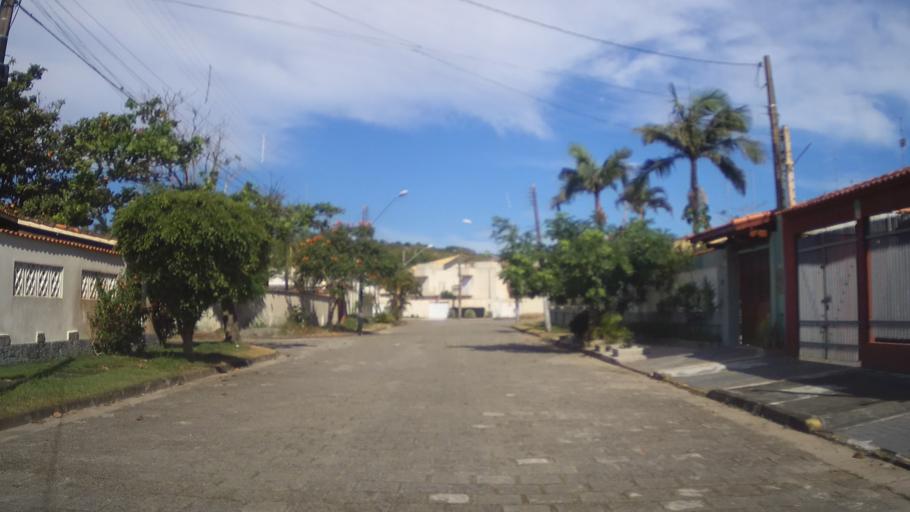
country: BR
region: Sao Paulo
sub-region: Itanhaem
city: Itanhaem
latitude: -24.1984
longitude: -46.8103
